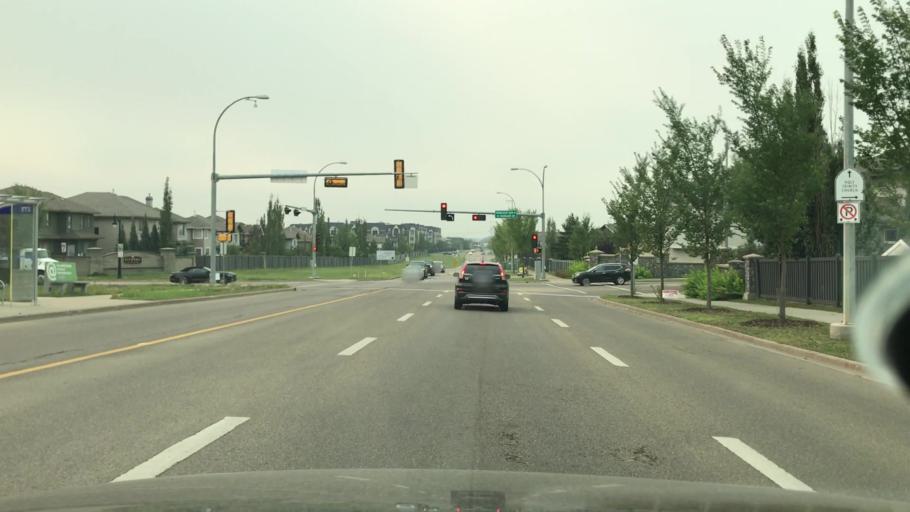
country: CA
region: Alberta
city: Edmonton
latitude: 53.4452
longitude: -113.5657
